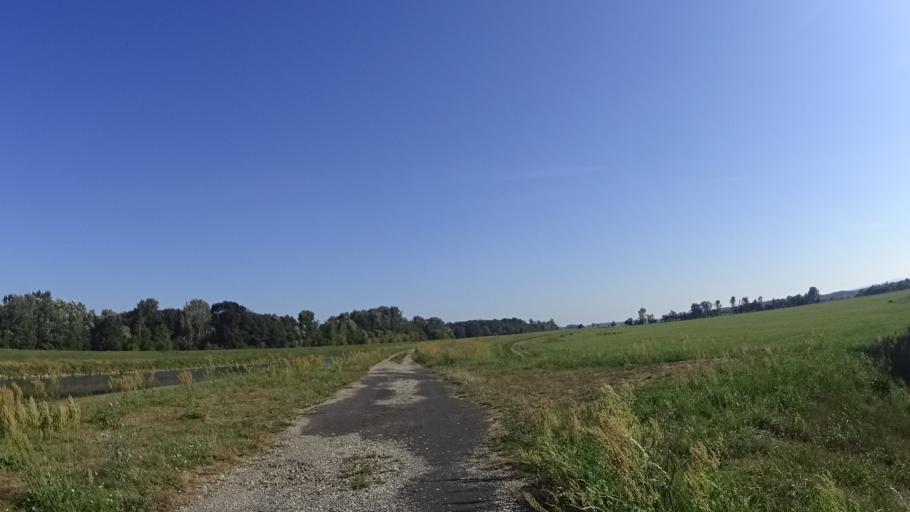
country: CZ
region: South Moravian
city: Tvrdonice
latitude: 48.7280
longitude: 17.0148
